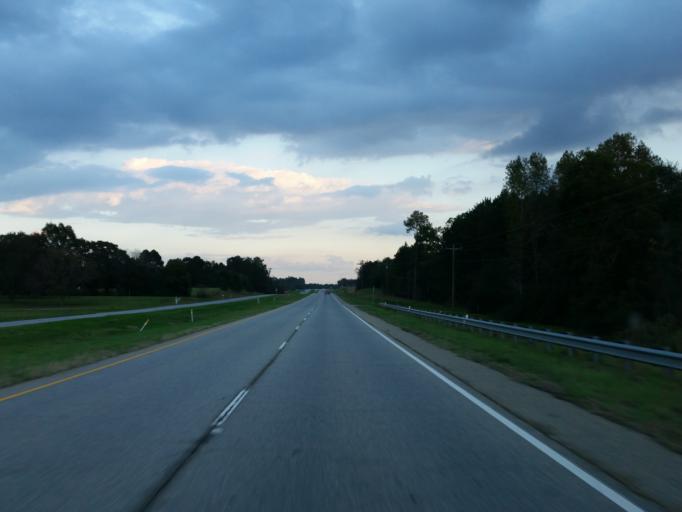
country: US
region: Georgia
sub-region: Pulaski County
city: Hawkinsville
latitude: 32.3127
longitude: -83.5227
